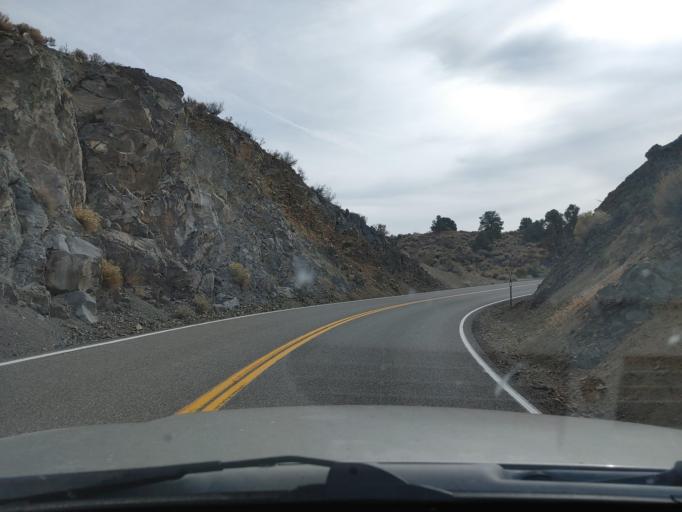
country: US
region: Nevada
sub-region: Storey County
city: Virginia City
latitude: 39.2680
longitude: -119.6298
